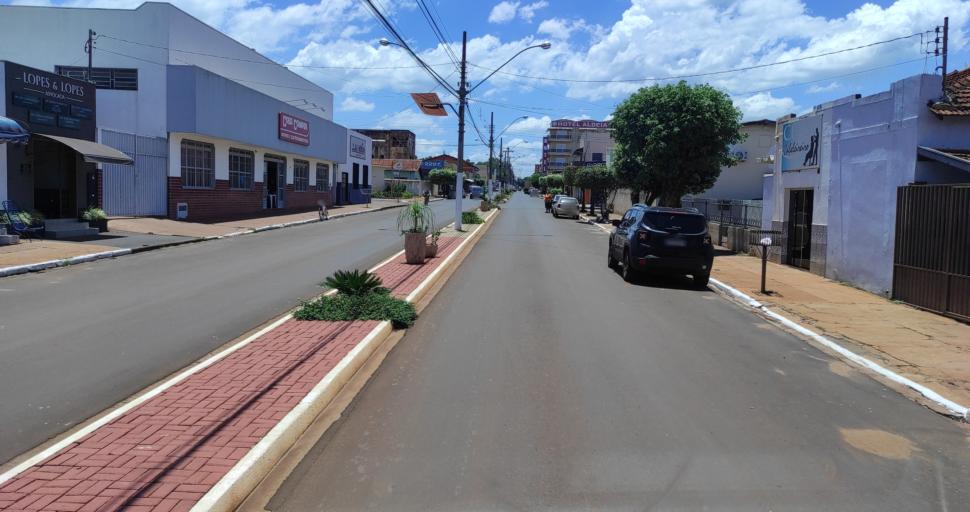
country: BR
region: Minas Gerais
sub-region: Frutal
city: Frutal
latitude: -20.1406
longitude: -48.7010
